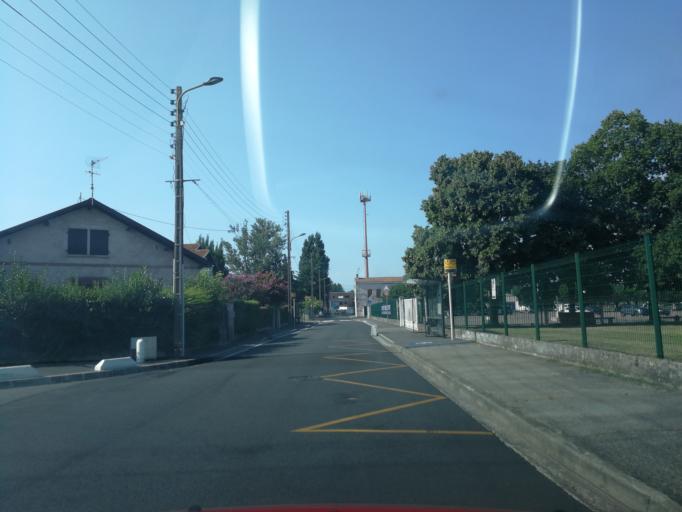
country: FR
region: Midi-Pyrenees
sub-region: Departement de la Haute-Garonne
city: Blagnac
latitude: 43.6214
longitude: 1.4082
